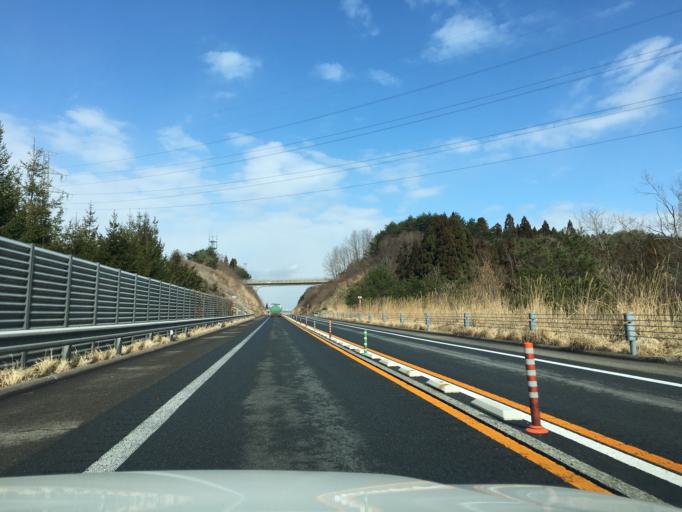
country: JP
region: Akita
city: Akita Shi
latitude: 39.8068
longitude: 140.0950
